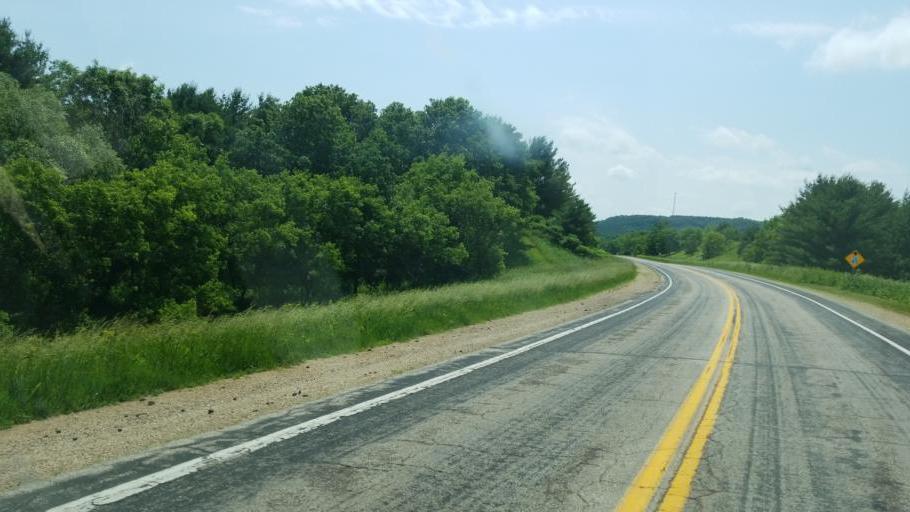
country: US
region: Wisconsin
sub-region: Monroe County
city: Cashton
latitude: 43.5849
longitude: -90.6372
